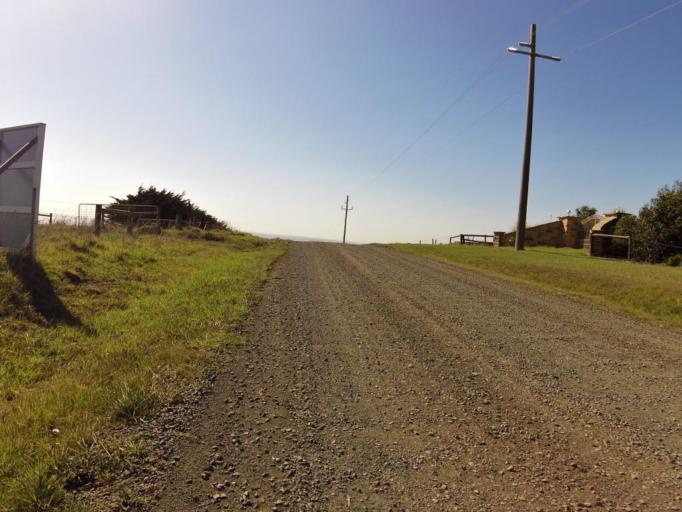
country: AU
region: Victoria
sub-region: Bass Coast
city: Phillip Island
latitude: -38.5313
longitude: 145.4079
